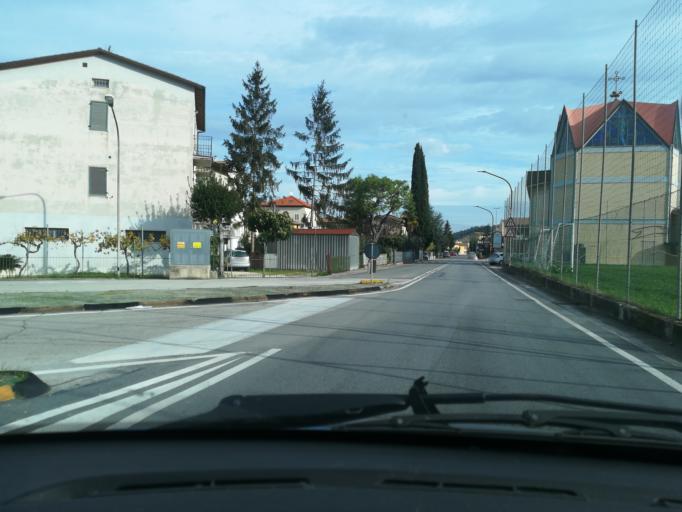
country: IT
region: The Marches
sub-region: Province of Fermo
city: Campiglione
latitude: 43.1692
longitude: 13.6784
